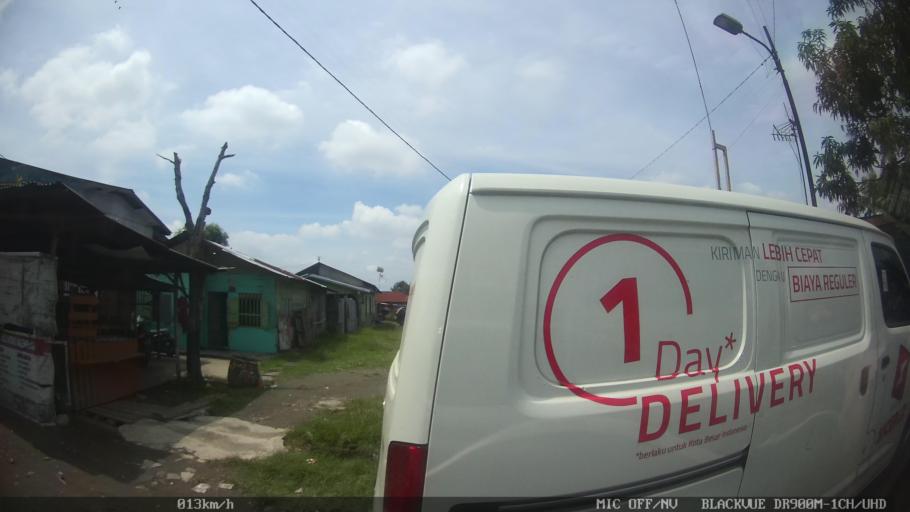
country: ID
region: North Sumatra
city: Medan
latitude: 3.6513
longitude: 98.6901
